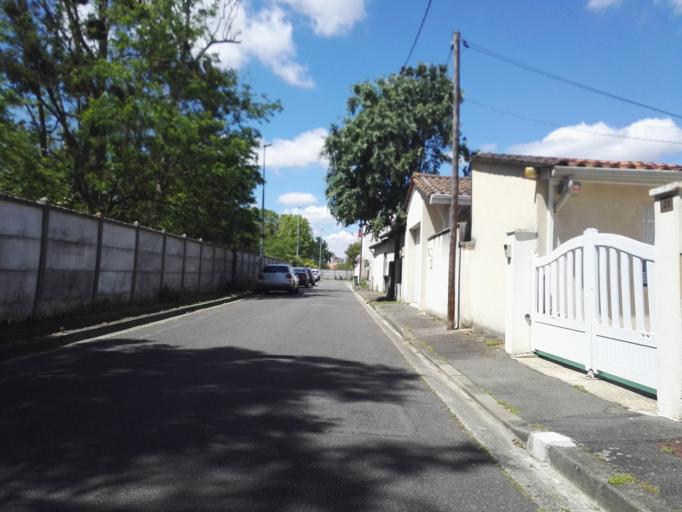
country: FR
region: Aquitaine
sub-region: Departement de la Gironde
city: Begles
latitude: 44.8030
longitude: -0.5670
